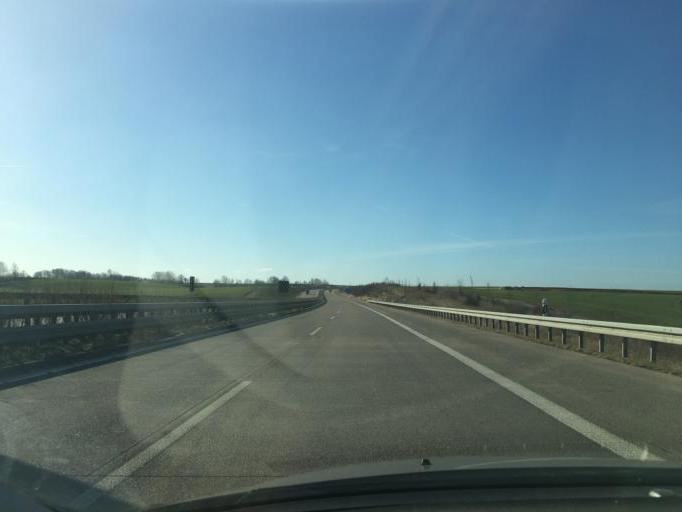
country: DE
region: Saxony
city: Narsdorf
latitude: 50.9897
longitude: 12.6928
